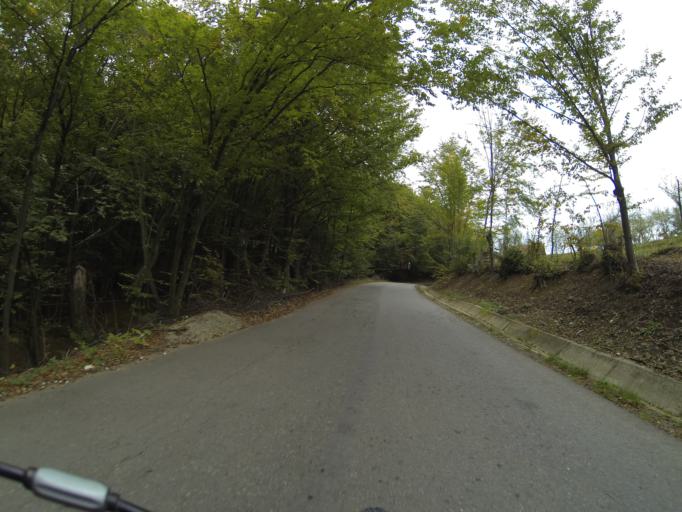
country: RO
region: Gorj
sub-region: Comuna Tismana
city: Pocruia
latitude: 45.0422
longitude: 22.9027
